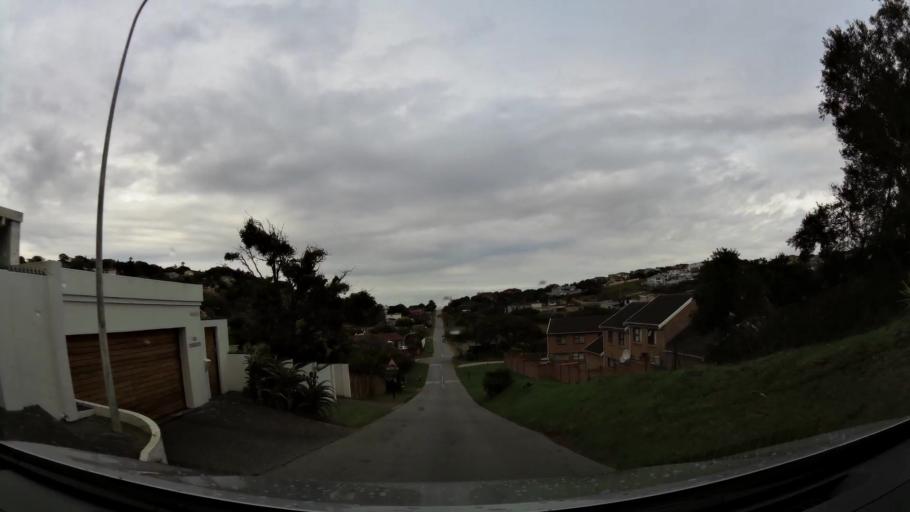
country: ZA
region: Eastern Cape
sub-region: Nelson Mandela Bay Metropolitan Municipality
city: Port Elizabeth
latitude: -34.0000
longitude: 25.5283
